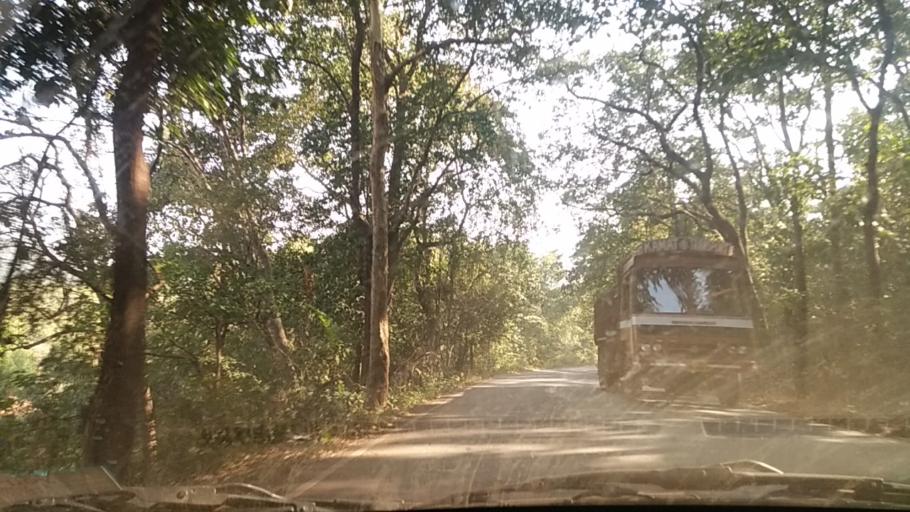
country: IN
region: Goa
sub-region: North Goa
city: Palle
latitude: 15.3866
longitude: 74.1249
